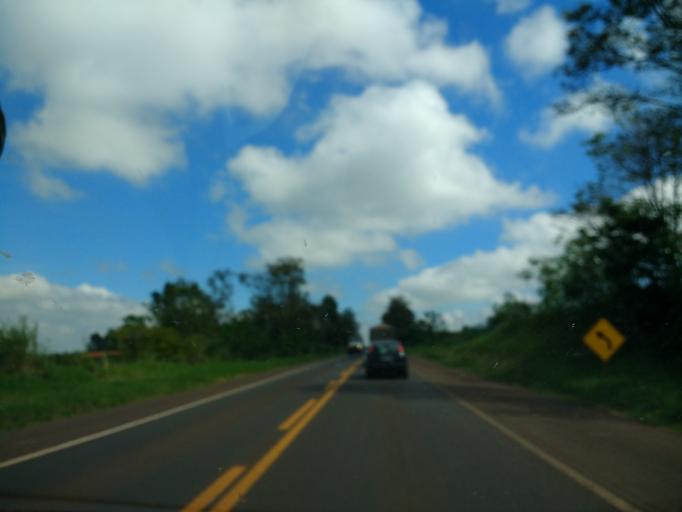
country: BR
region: Parana
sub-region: Cruzeiro Do Oeste
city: Cruzeiro do Oeste
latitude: -23.7680
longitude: -53.1543
